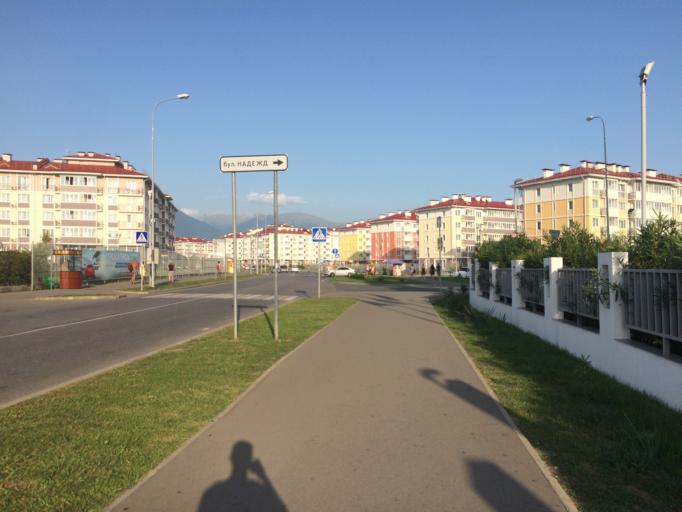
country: RU
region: Krasnodarskiy
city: Vysokoye
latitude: 43.3910
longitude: 39.9897
